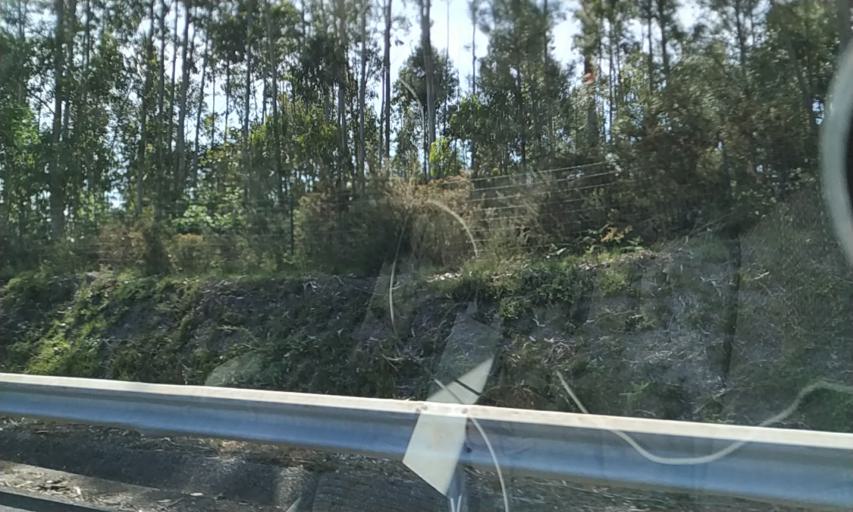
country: ES
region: Galicia
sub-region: Provincia da Coruna
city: Padron
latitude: 42.7769
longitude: -8.6419
